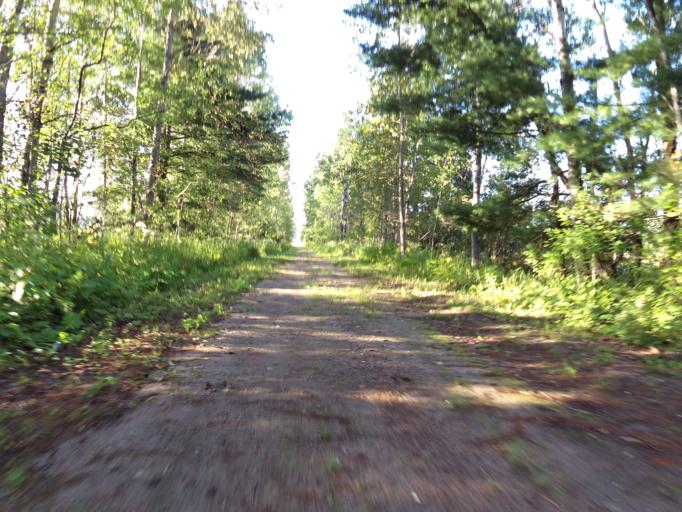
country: CA
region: Quebec
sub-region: Outaouais
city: Maniwaki
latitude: 46.3000
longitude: -76.0235
